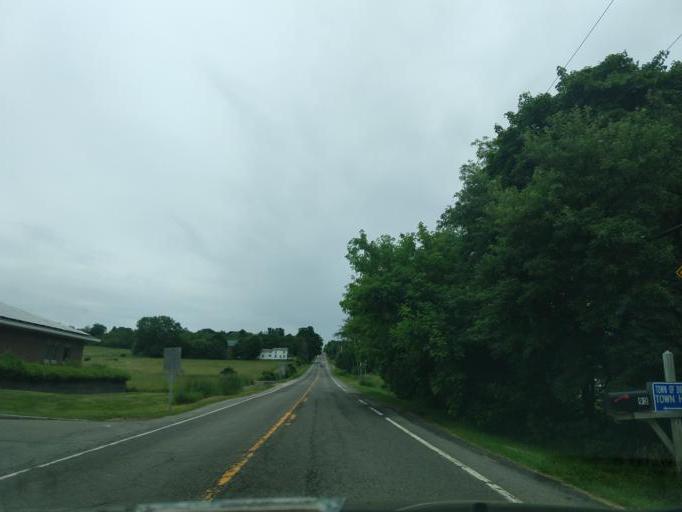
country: US
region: New York
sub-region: Tompkins County
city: Dryden
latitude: 42.4909
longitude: -76.2866
